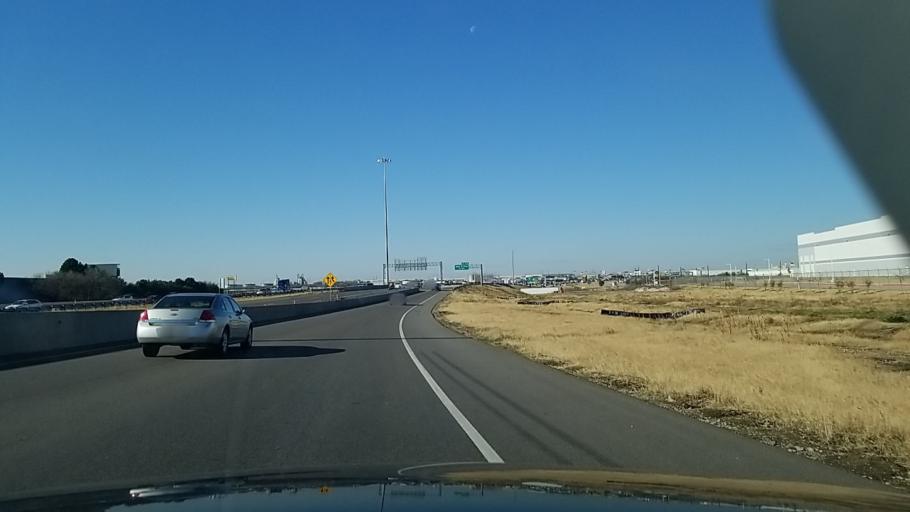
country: US
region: Texas
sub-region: Tarrant County
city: Blue Mound
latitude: 32.8401
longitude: -97.3175
